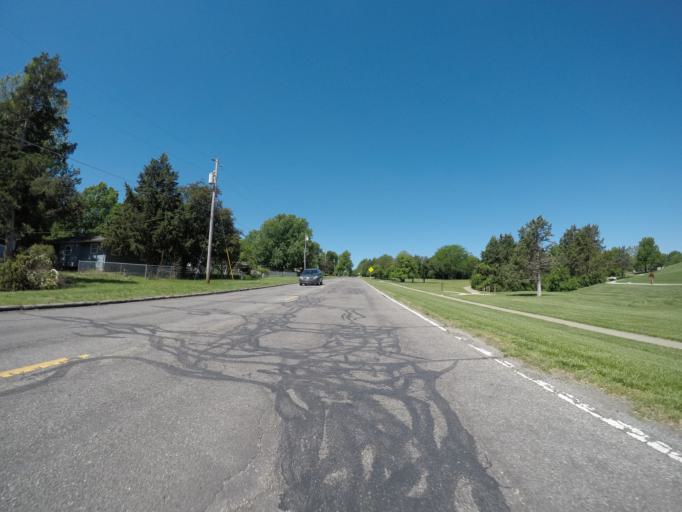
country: US
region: Kansas
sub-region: Riley County
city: Manhattan
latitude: 39.1964
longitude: -96.6195
